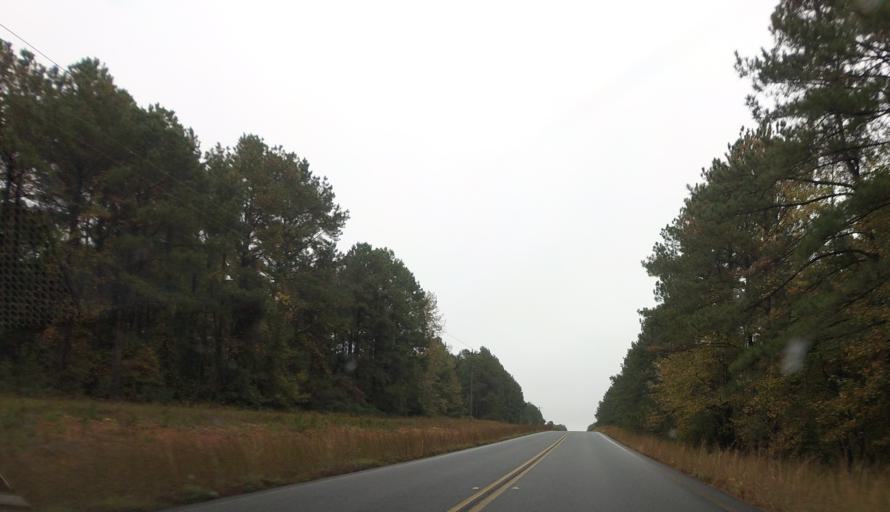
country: US
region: Georgia
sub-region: Marion County
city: Buena Vista
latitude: 32.3931
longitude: -84.4261
